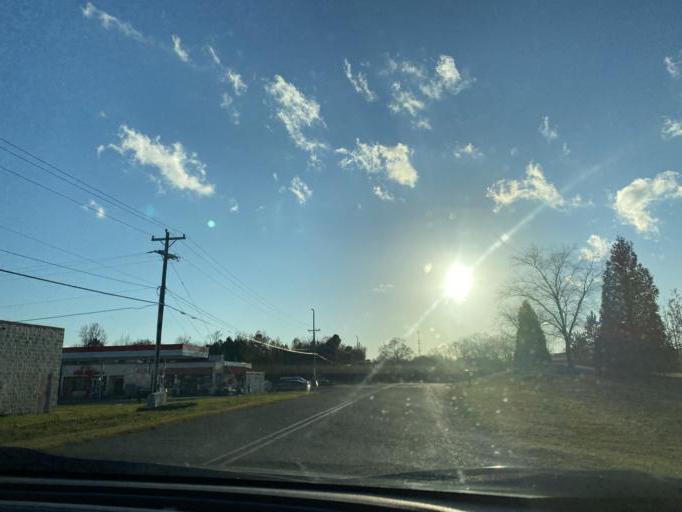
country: US
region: South Carolina
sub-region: York County
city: Clover
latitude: 35.1298
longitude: -81.2172
